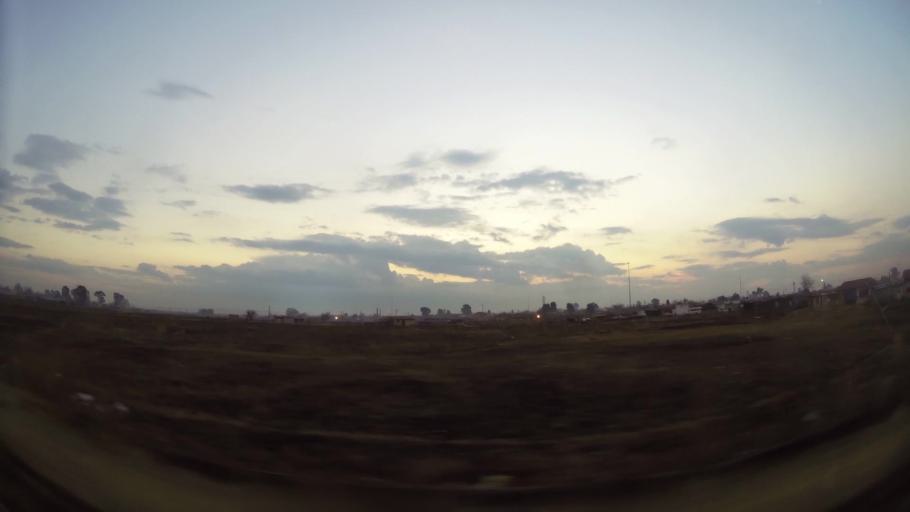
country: ZA
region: Gauteng
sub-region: City of Johannesburg Metropolitan Municipality
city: Orange Farm
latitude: -26.5413
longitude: 27.8442
